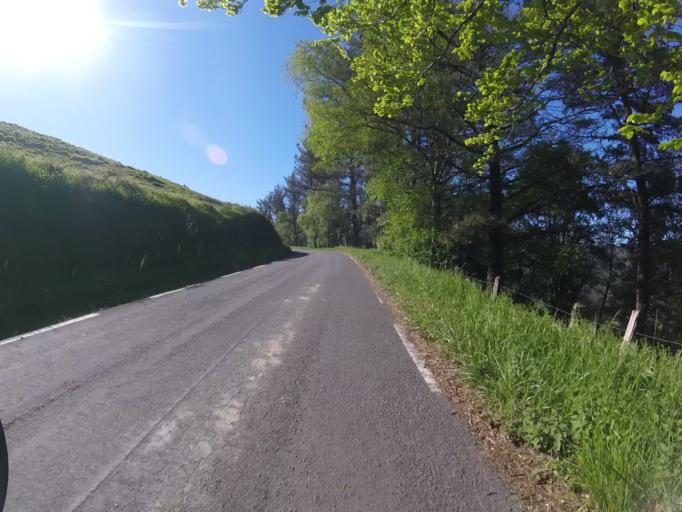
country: ES
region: Basque Country
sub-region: Provincia de Guipuzcoa
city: Aizarnazabal
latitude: 43.2156
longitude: -2.2092
